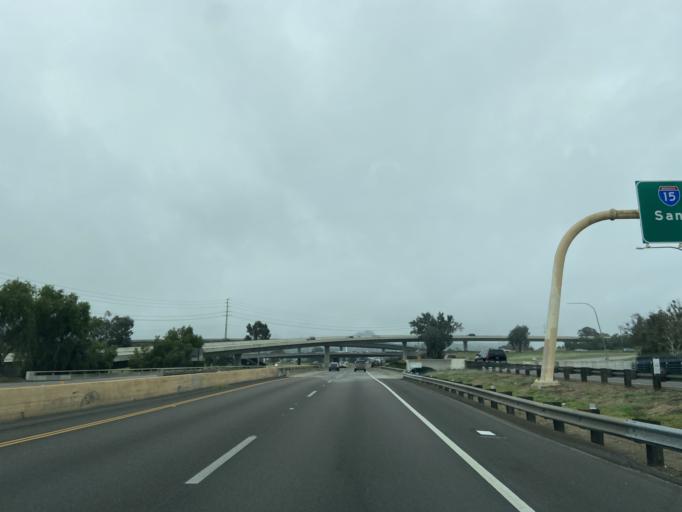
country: US
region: California
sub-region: San Diego County
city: Escondido
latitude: 33.1281
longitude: -117.1017
